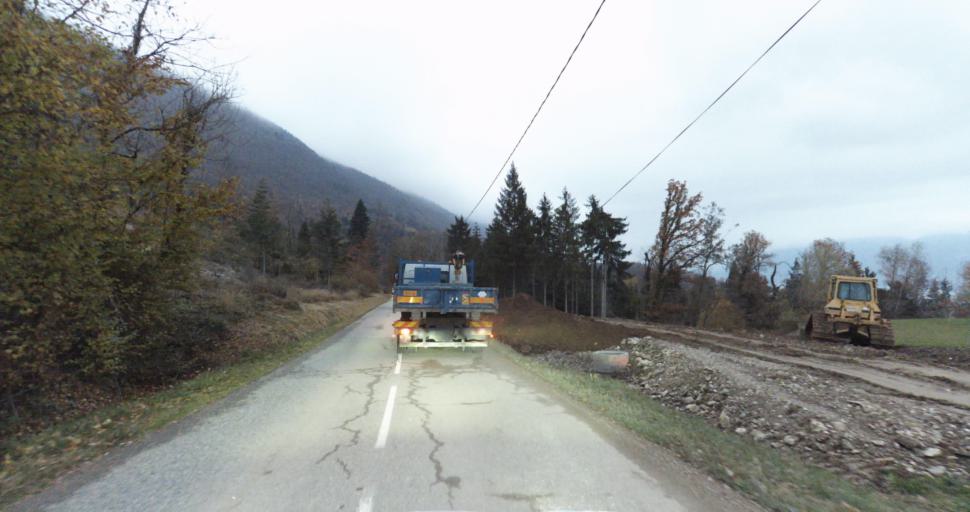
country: FR
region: Rhone-Alpes
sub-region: Departement de la Haute-Savoie
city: Saint-Jorioz
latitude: 45.8155
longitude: 6.1377
